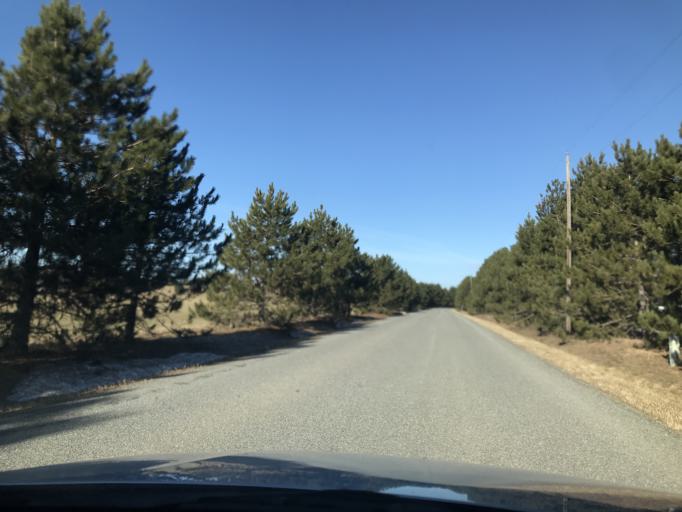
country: US
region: Wisconsin
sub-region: Marinette County
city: Niagara
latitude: 45.3794
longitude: -88.0310
